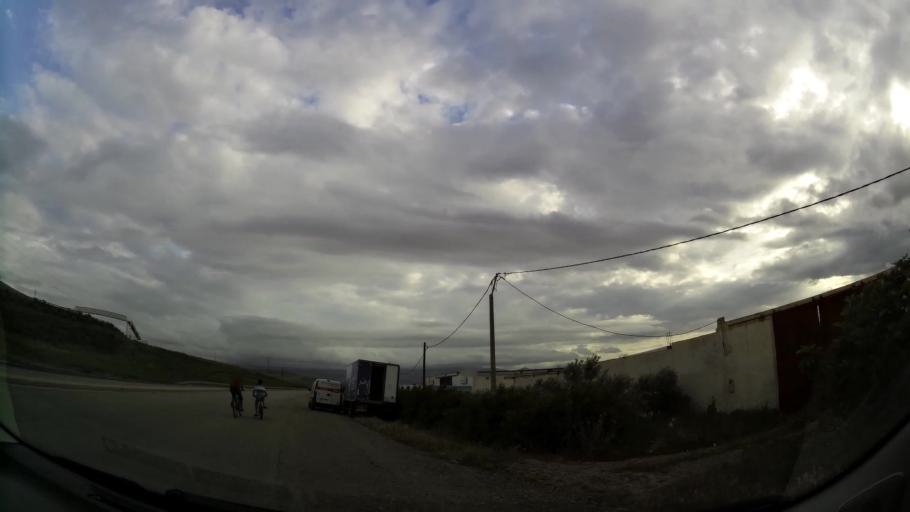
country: MA
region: Taza-Al Hoceima-Taounate
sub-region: Taza
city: Taza
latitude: 34.2666
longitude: -3.9572
